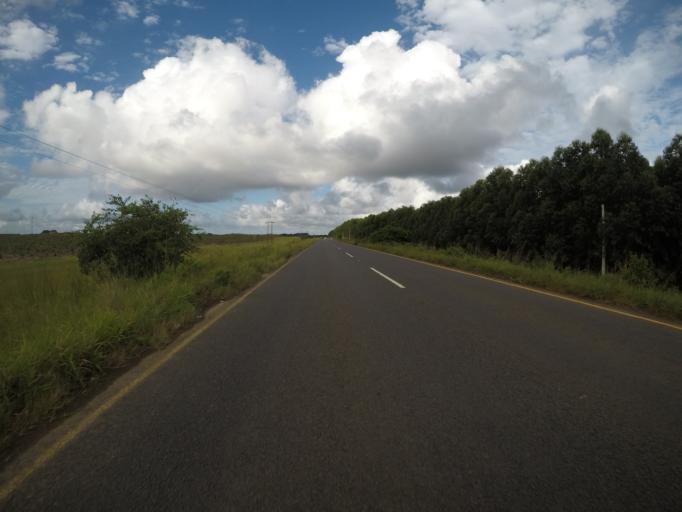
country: ZA
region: KwaZulu-Natal
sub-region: uMkhanyakude District Municipality
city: Mtubatuba
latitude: -28.3854
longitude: 32.2372
